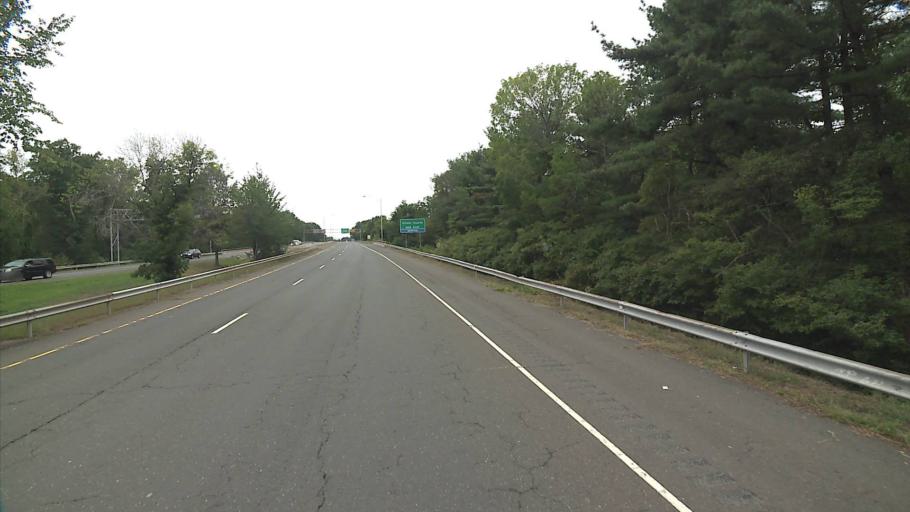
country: US
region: Connecticut
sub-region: Hartford County
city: Farmington
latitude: 41.7238
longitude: -72.7990
